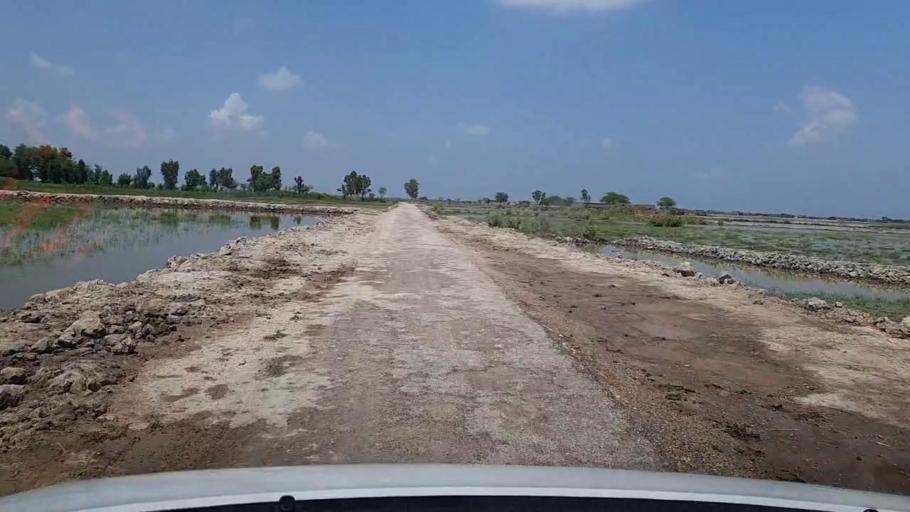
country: PK
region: Sindh
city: Bhiria
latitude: 26.9803
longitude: 68.2165
